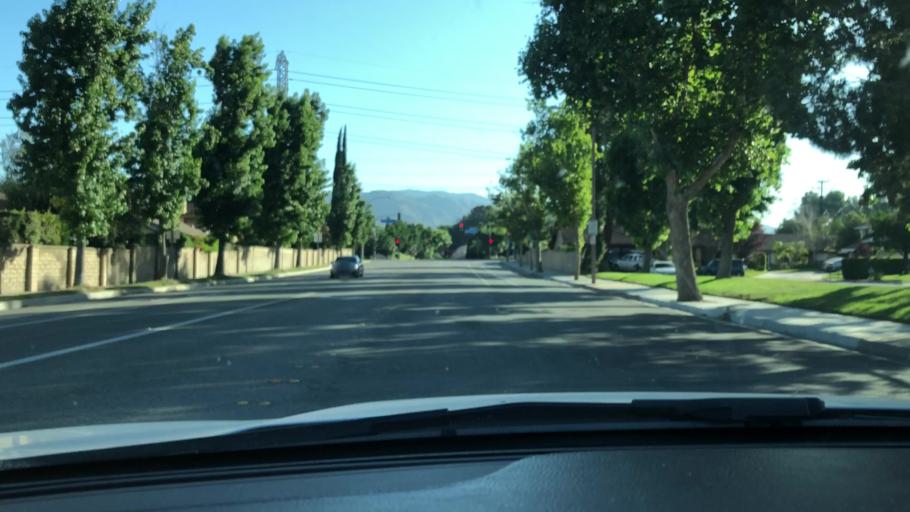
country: US
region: California
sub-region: Los Angeles County
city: Santa Clarita
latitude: 34.3884
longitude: -118.5445
